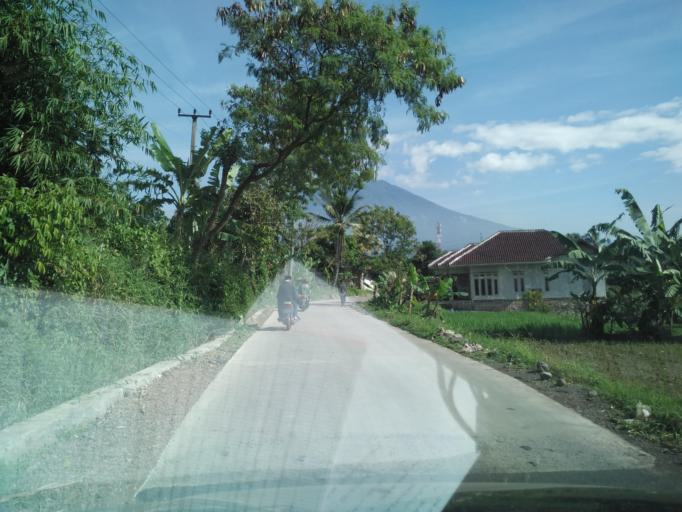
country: ID
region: West Java
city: Cibeber
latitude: -6.8600
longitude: 107.0748
